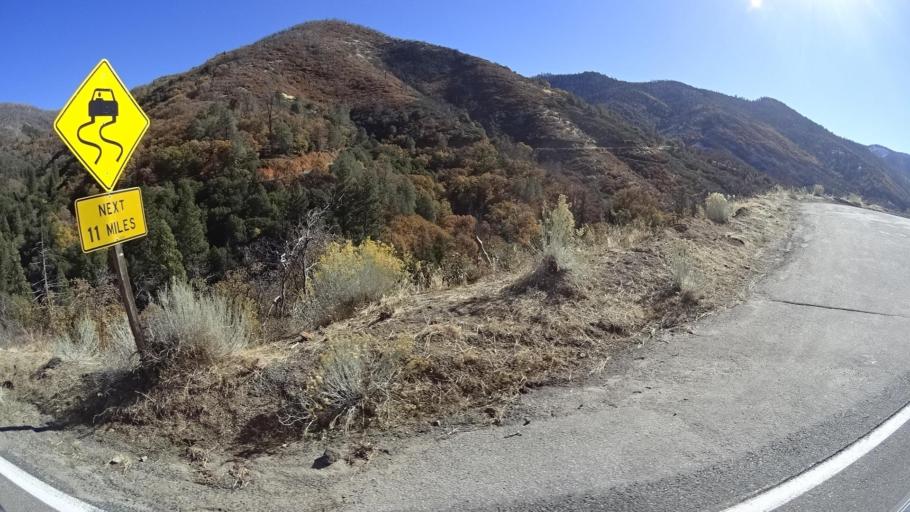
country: US
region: California
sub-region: Kern County
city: Alta Sierra
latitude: 35.7471
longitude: -118.5857
